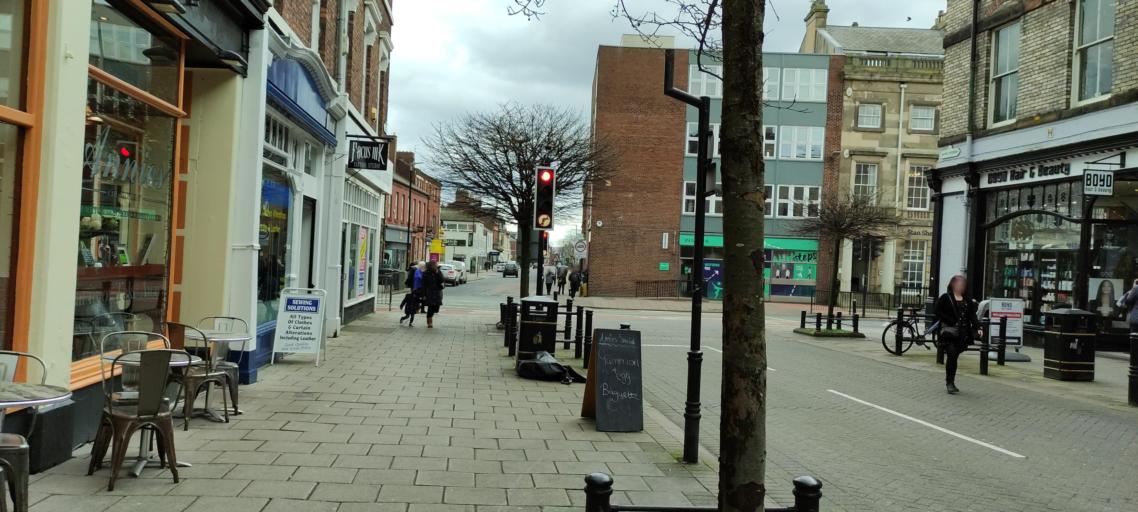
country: GB
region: England
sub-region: Cumbria
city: Carlisle
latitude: 54.8939
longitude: -2.9338
